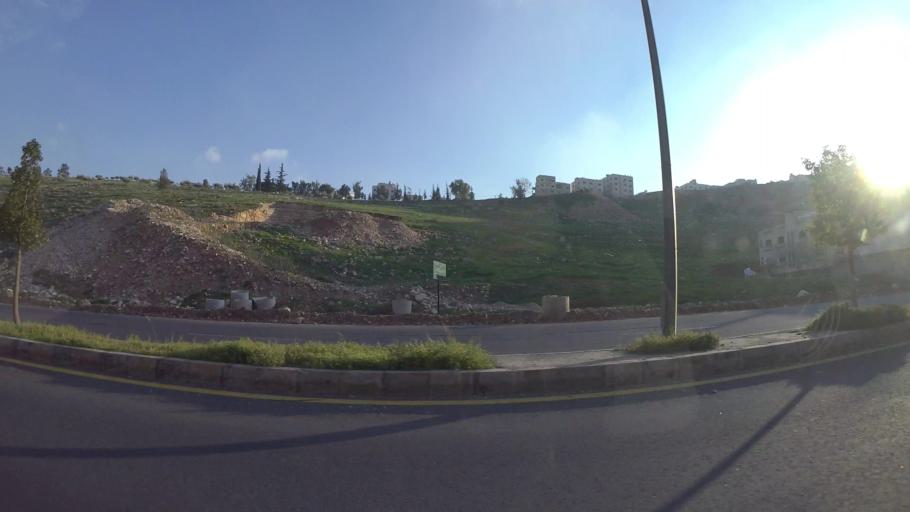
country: JO
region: Amman
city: Amman
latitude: 31.9817
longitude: 35.9618
